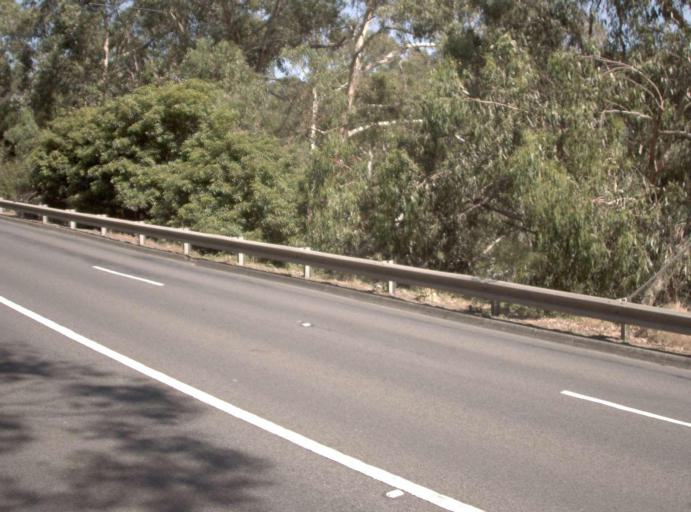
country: AU
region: Victoria
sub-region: Yarra Ranges
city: Tremont
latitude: -37.8986
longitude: 145.3228
